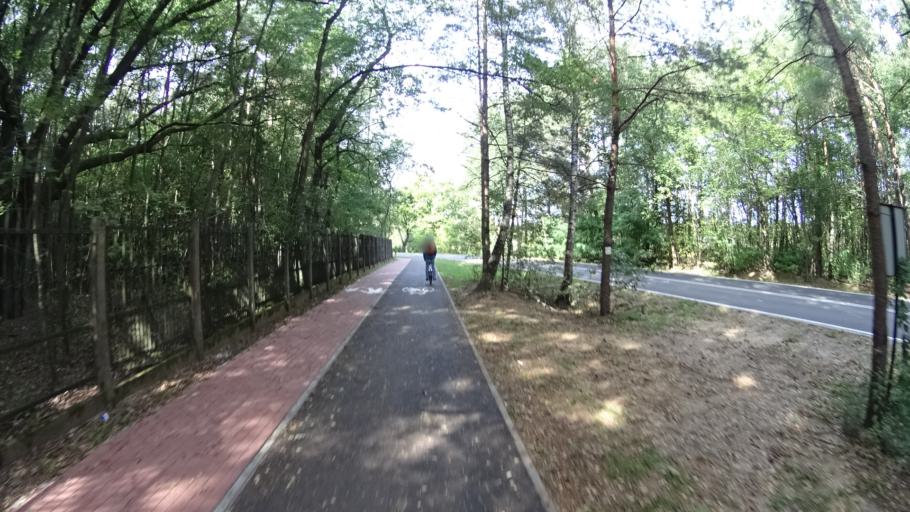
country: PL
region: Masovian Voivodeship
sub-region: Powiat legionowski
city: Bialobrzegi
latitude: 52.4690
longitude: 21.0737
